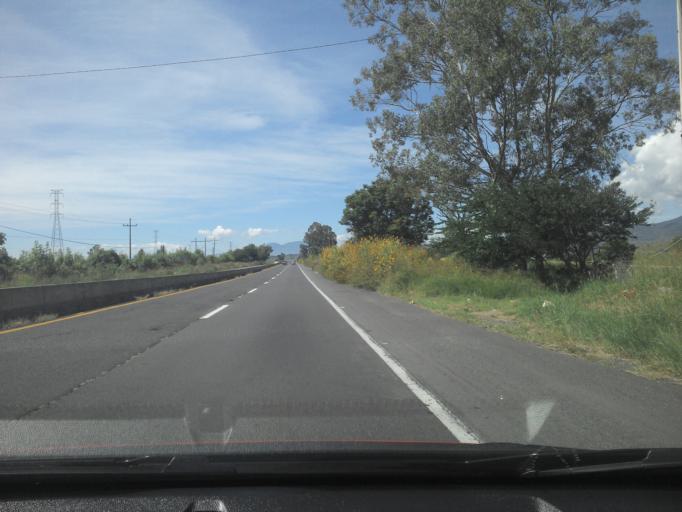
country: MX
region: Jalisco
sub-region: Tala
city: Los Ruisenores
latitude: 20.7108
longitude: -103.6635
